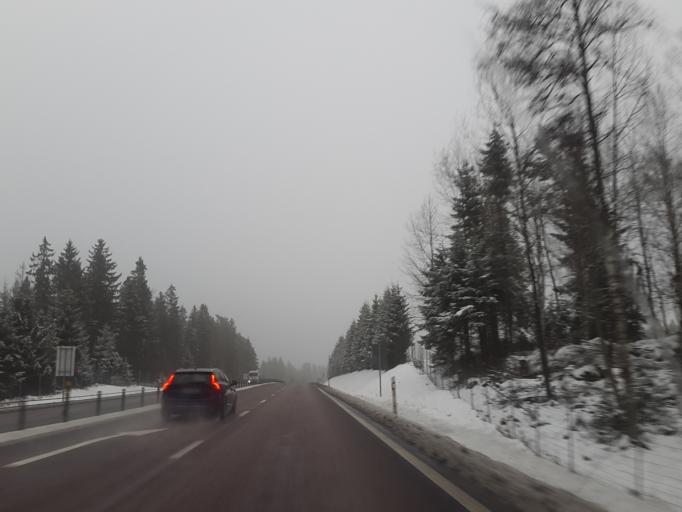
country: SE
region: Joenkoeping
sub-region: Mullsjo Kommun
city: Mullsjoe
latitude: 57.7547
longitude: 13.9274
